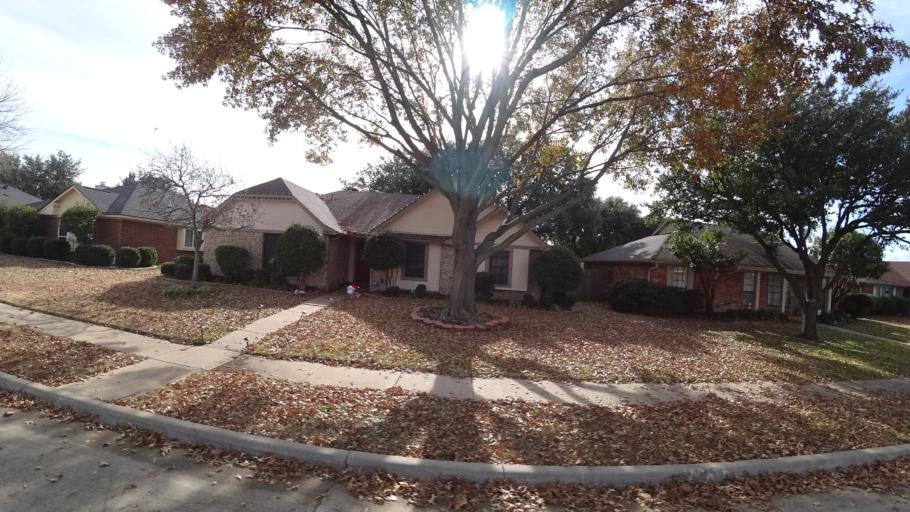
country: US
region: Texas
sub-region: Denton County
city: Highland Village
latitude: 33.0614
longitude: -97.0431
